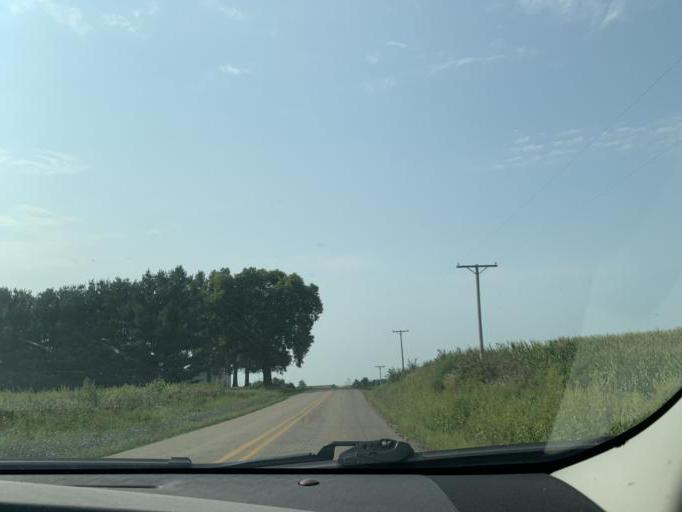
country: US
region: Illinois
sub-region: Whiteside County
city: Morrison
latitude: 41.8510
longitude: -89.8719
